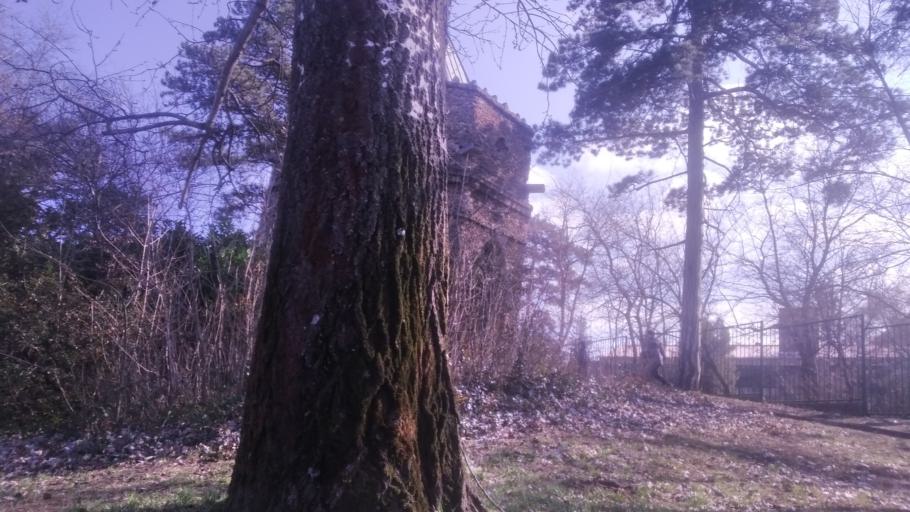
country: HU
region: Komarom-Esztergom
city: Tata
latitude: 47.6486
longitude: 18.3364
